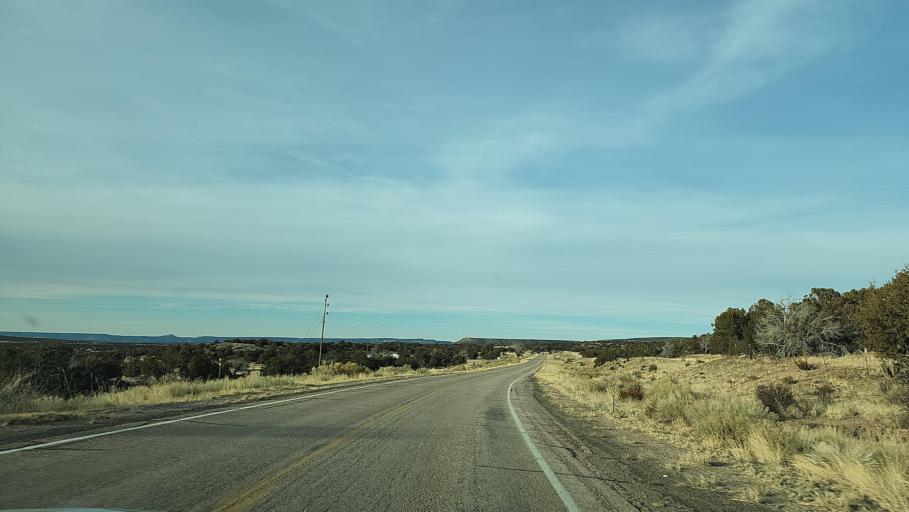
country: US
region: New Mexico
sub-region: McKinley County
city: Black Rock
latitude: 34.4188
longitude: -108.4304
